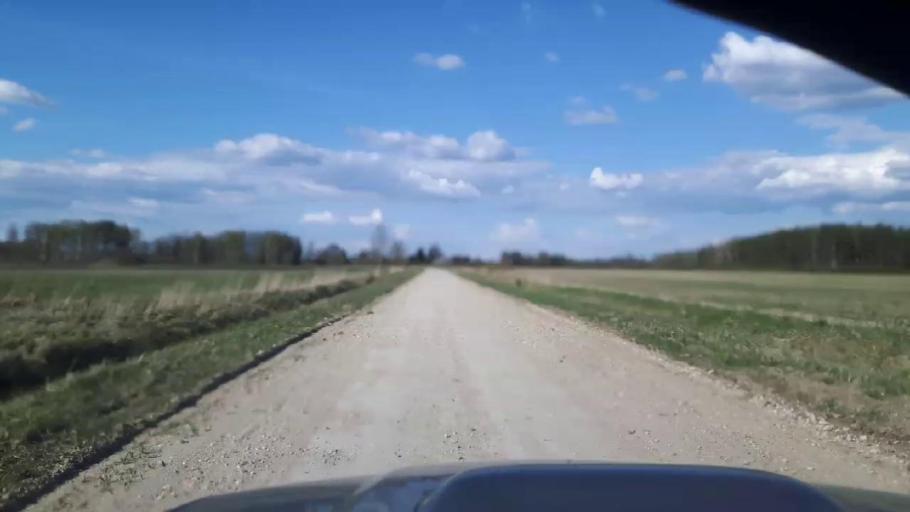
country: EE
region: Paernumaa
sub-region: Tootsi vald
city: Tootsi
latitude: 58.4452
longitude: 24.8580
